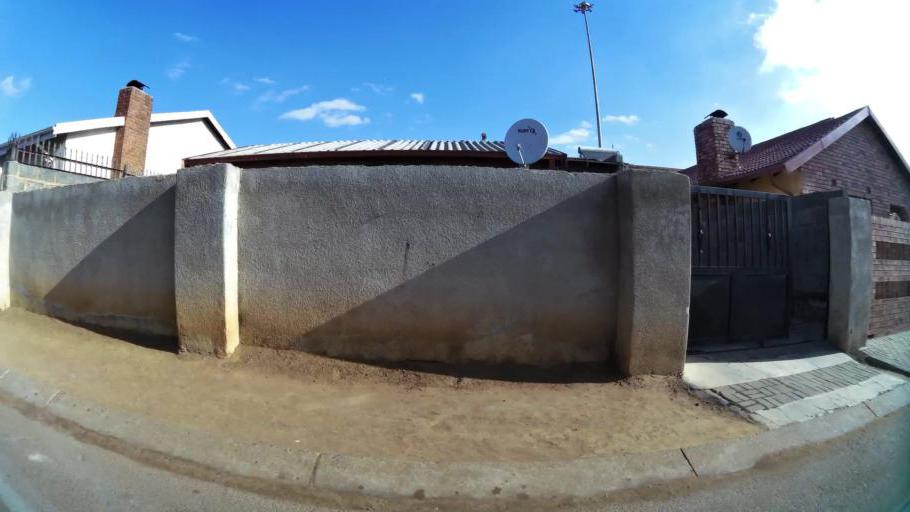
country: ZA
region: Gauteng
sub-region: City of Johannesburg Metropolitan Municipality
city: Soweto
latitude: -26.2540
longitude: 27.9100
